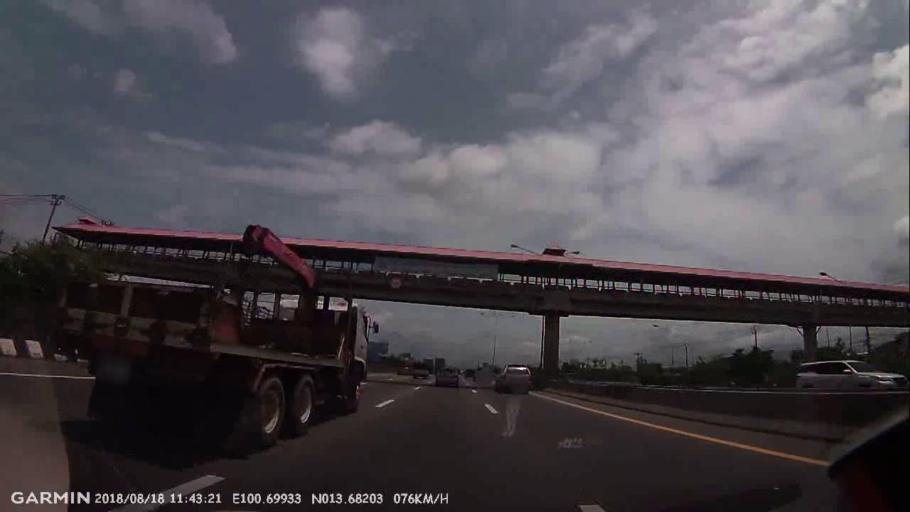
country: TH
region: Bangkok
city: Bang Na
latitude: 13.6827
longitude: 100.6993
